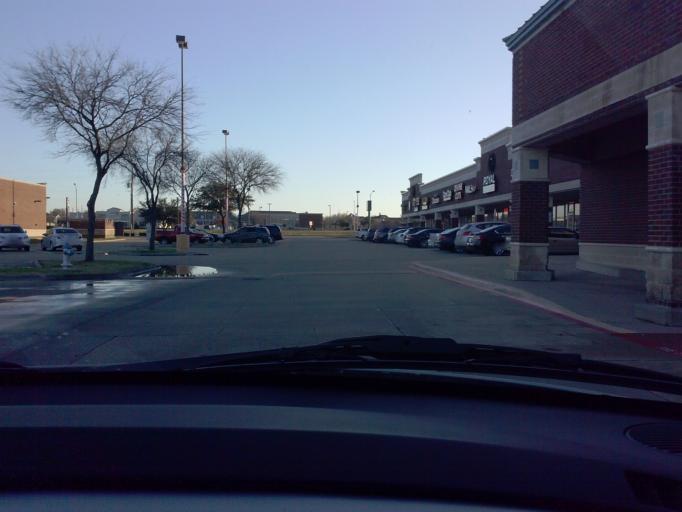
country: US
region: Texas
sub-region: Collin County
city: Plano
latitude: 33.0578
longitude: -96.7718
